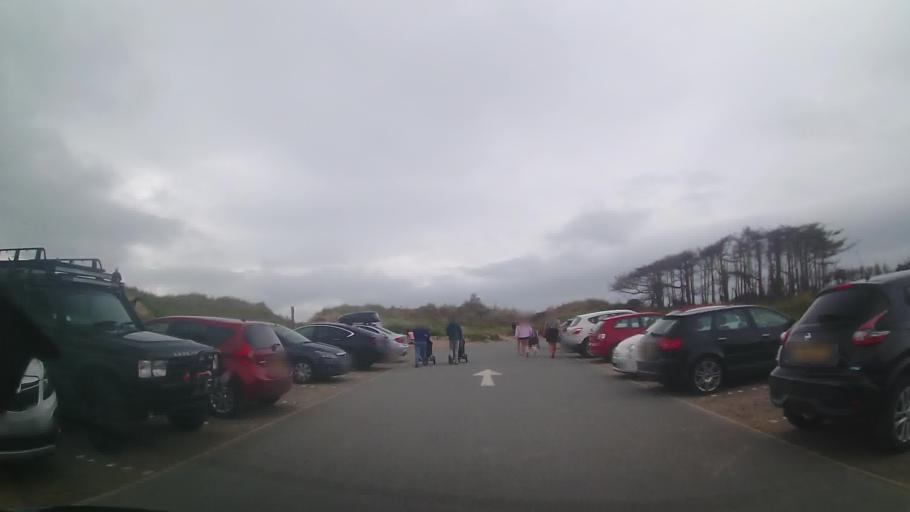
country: GB
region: Wales
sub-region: Gwynedd
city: Caernarfon
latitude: 53.1441
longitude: -4.3849
